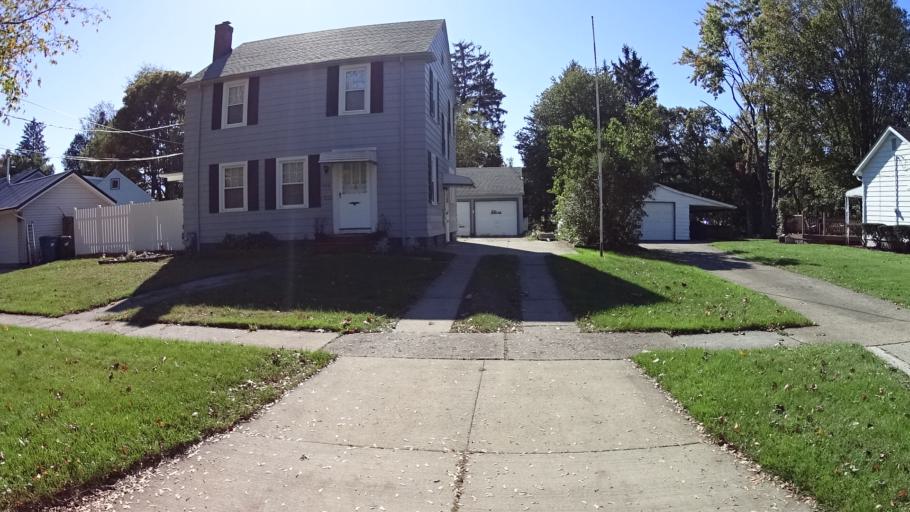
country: US
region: Ohio
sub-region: Lorain County
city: Amherst
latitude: 41.4012
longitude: -82.2290
